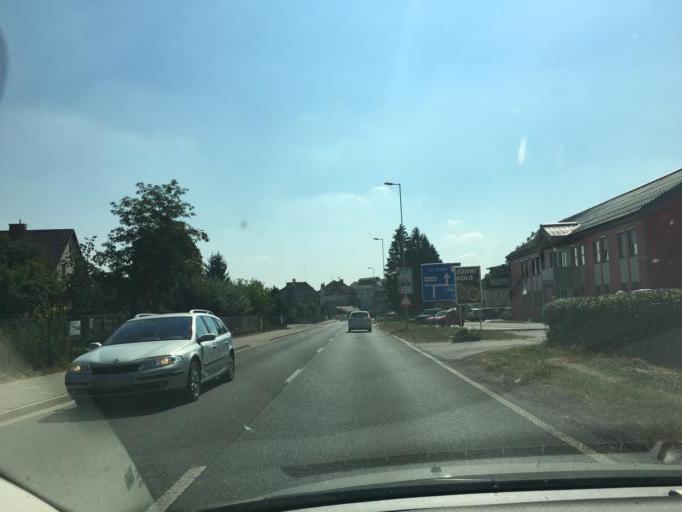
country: CZ
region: Kralovehradecky
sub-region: Okres Trutnov
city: Vrchlabi
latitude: 50.6201
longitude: 15.6065
